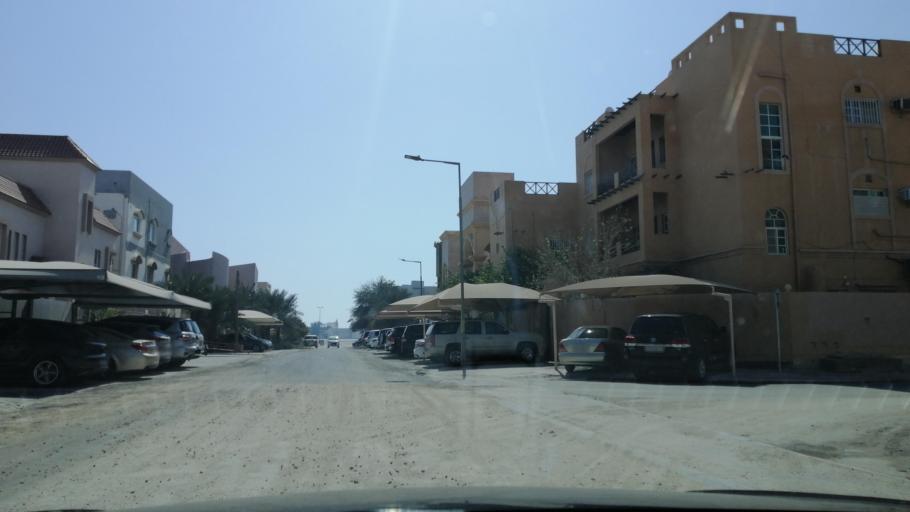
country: BH
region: Muharraq
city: Al Hadd
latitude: 26.2480
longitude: 50.6366
